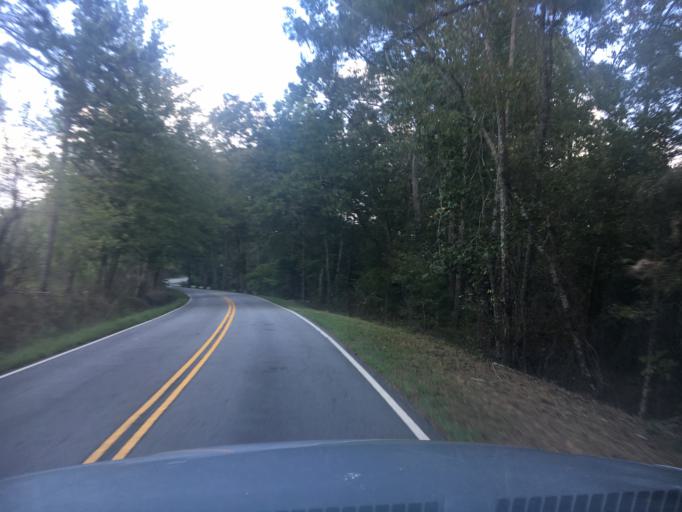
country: US
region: South Carolina
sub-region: Pickens County
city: Liberty
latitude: 34.7128
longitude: -82.7029
